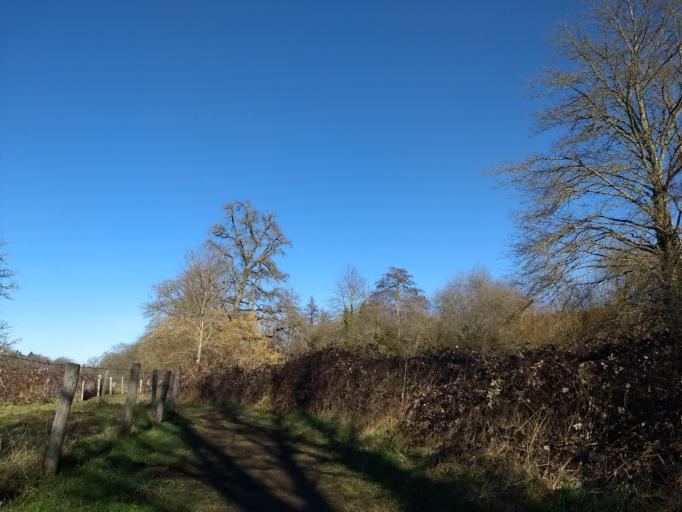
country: FR
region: Limousin
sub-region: Departement de la Haute-Vienne
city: Isle
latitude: 45.8235
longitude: 1.2107
